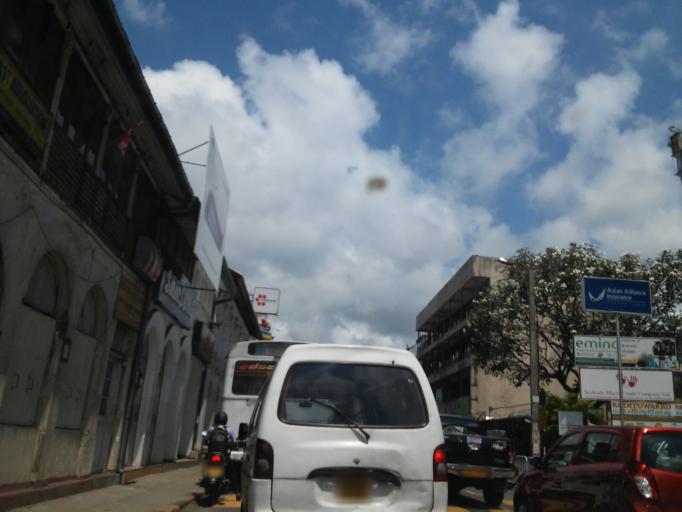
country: LK
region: Central
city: Kandy
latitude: 7.2967
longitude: 80.6375
